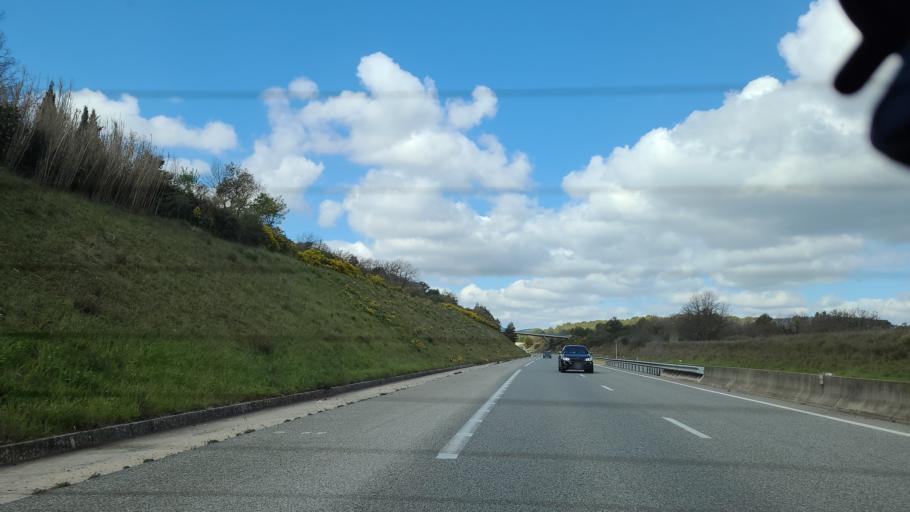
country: FR
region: Provence-Alpes-Cote d'Azur
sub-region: Departement du Var
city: Carnoules
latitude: 43.2903
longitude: 6.2067
